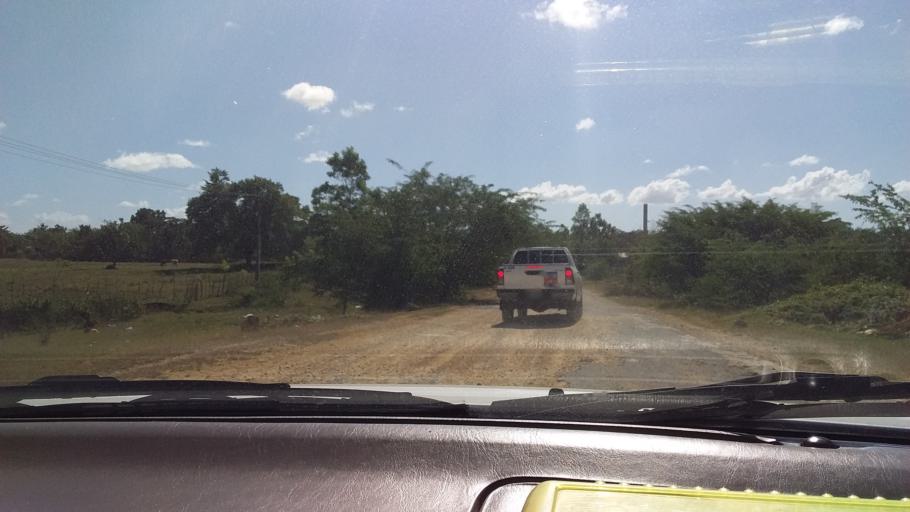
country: DO
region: Santo Domingo
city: Guerra
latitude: 18.5687
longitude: -69.7843
